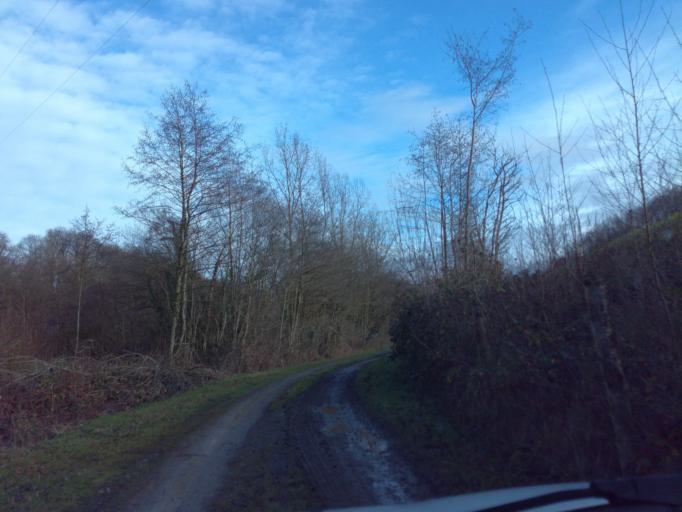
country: FR
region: Brittany
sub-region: Departement d'Ille-et-Vilaine
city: Liffre
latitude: 48.1964
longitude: -1.4772
